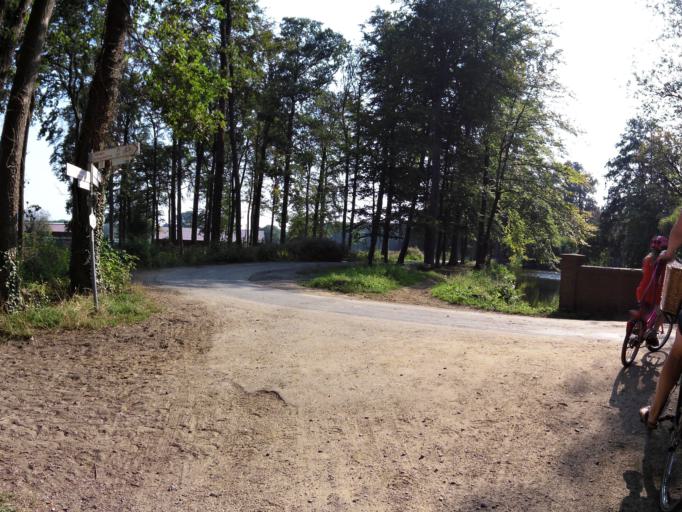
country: DE
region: North Rhine-Westphalia
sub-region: Regierungsbezirk Munster
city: Havixbeck
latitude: 51.9733
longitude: 7.4420
